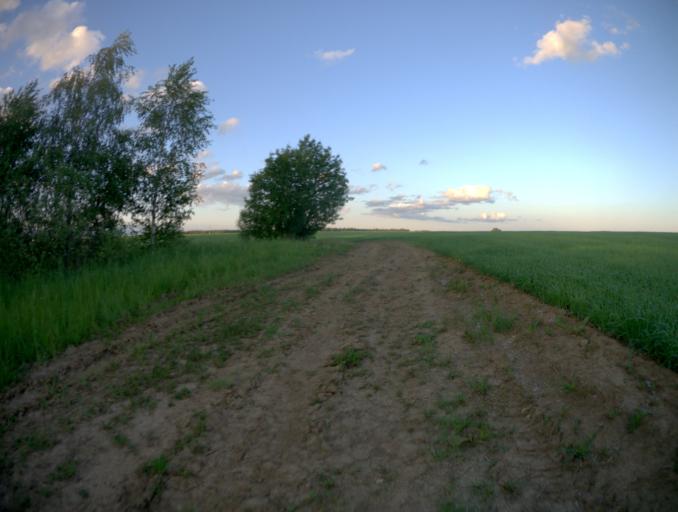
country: RU
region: Ivanovo
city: Gavrilov Posad
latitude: 56.5402
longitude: 40.1989
